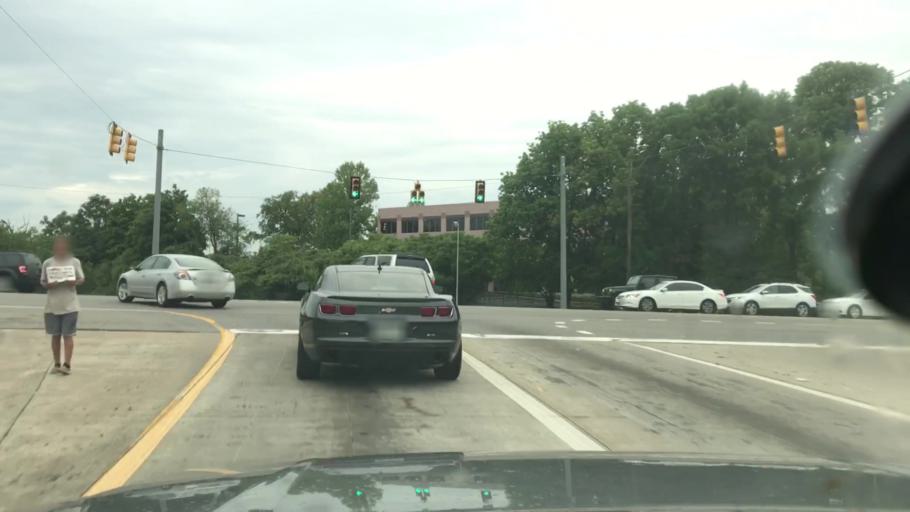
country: US
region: Tennessee
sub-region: Davidson County
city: Lakewood
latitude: 36.1685
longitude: -86.6902
